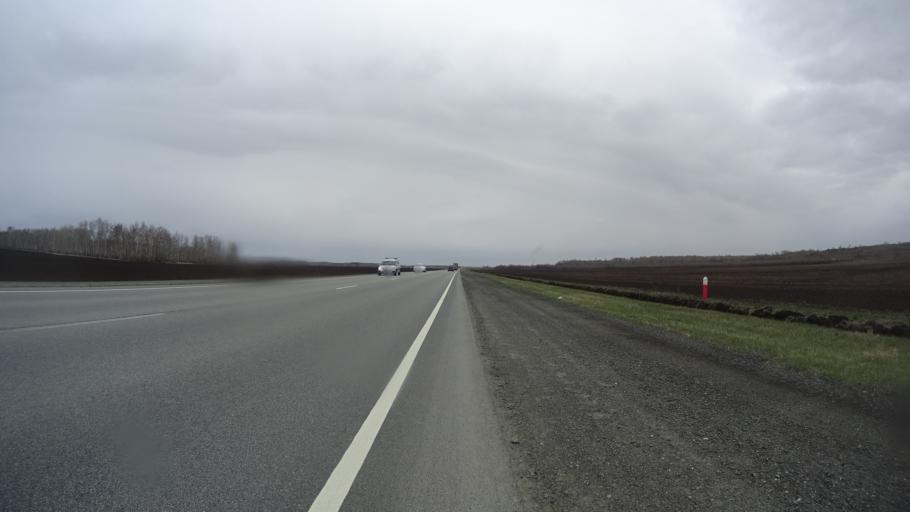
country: RU
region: Chelyabinsk
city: Krasnogorskiy
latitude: 54.5762
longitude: 61.2913
